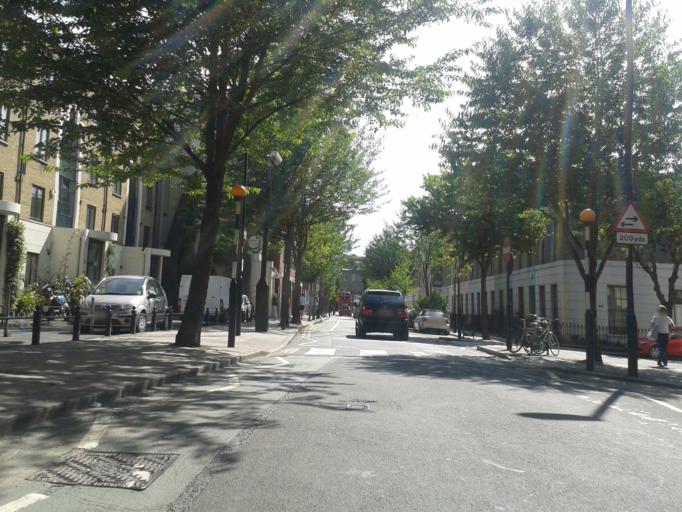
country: GB
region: England
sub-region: Greater London
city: Barnsbury
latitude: 51.5337
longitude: -0.1213
